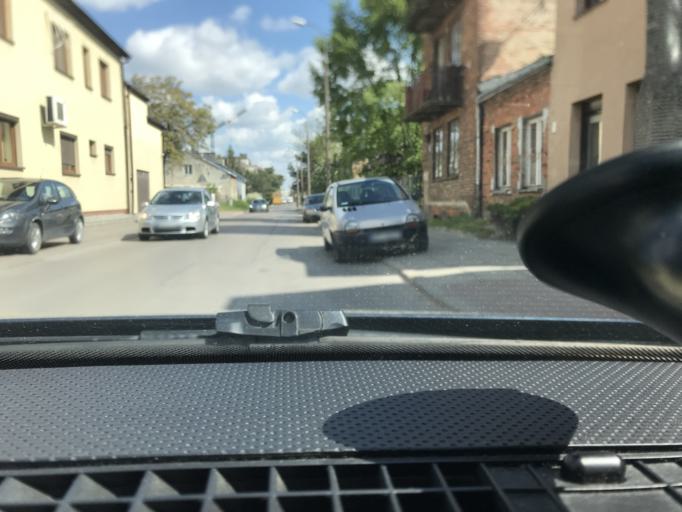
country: PL
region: Masovian Voivodeship
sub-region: Powiat pruszkowski
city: Pruszkow
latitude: 52.1604
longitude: 20.7910
